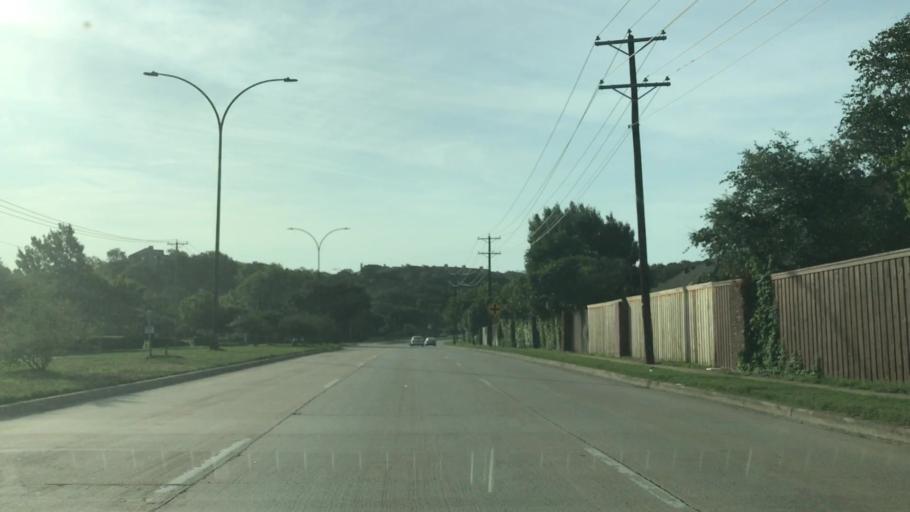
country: US
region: Texas
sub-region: Tarrant County
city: Arlington
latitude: 32.7818
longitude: -97.0885
